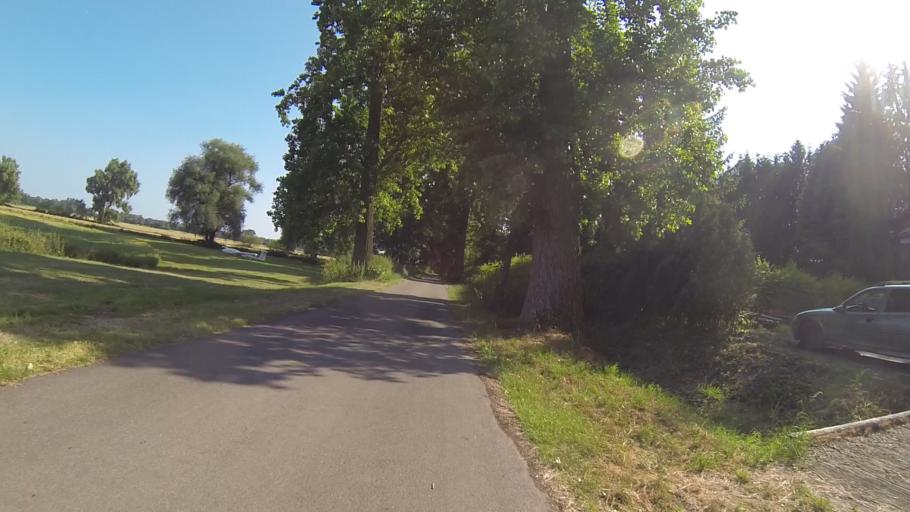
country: DE
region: Baden-Wuerttemberg
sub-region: Tuebingen Region
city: Erbach
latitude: 48.3407
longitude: 9.9119
